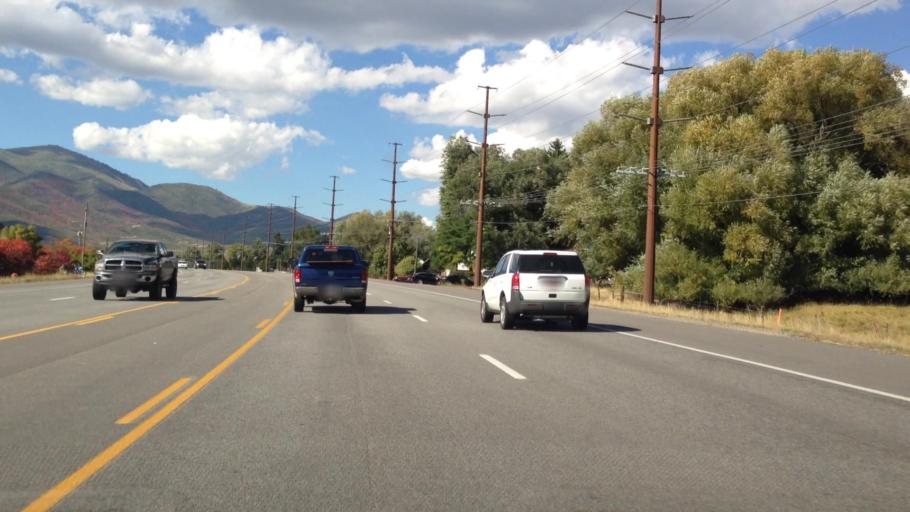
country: US
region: Utah
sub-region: Wasatch County
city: Heber
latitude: 40.5349
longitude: -111.4099
